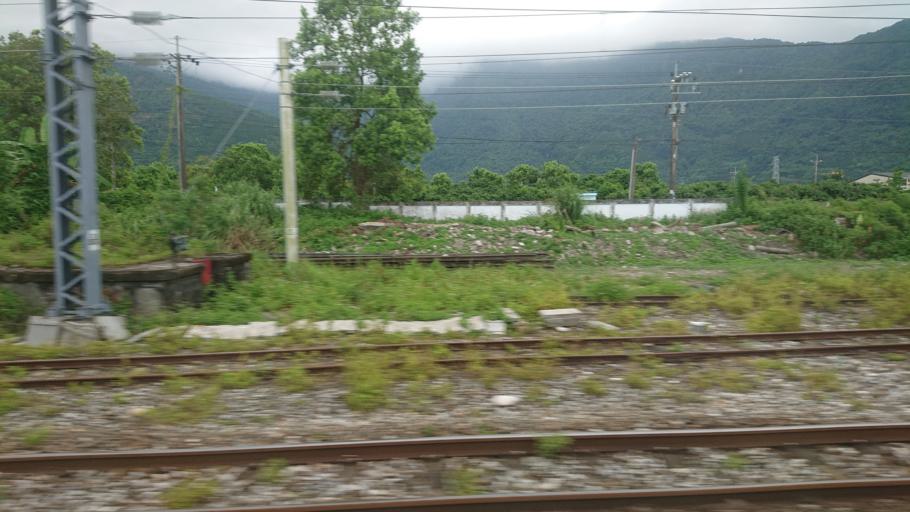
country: TW
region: Taiwan
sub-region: Hualien
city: Hualian
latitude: 23.7450
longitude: 121.4460
